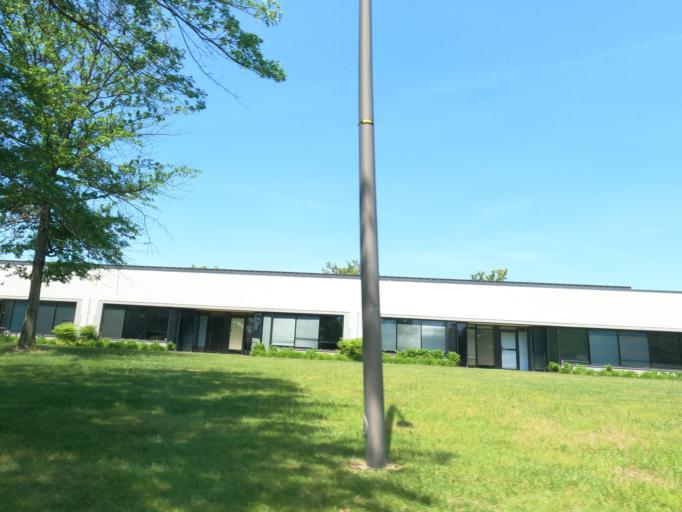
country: US
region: Maryland
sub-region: Anne Arundel County
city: Jessup
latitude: 39.1806
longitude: -76.8065
